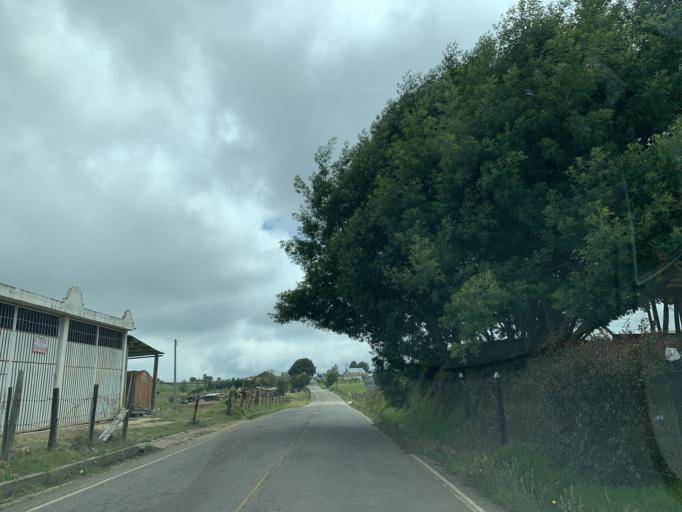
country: CO
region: Boyaca
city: Tunja
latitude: 5.5832
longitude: -73.3496
